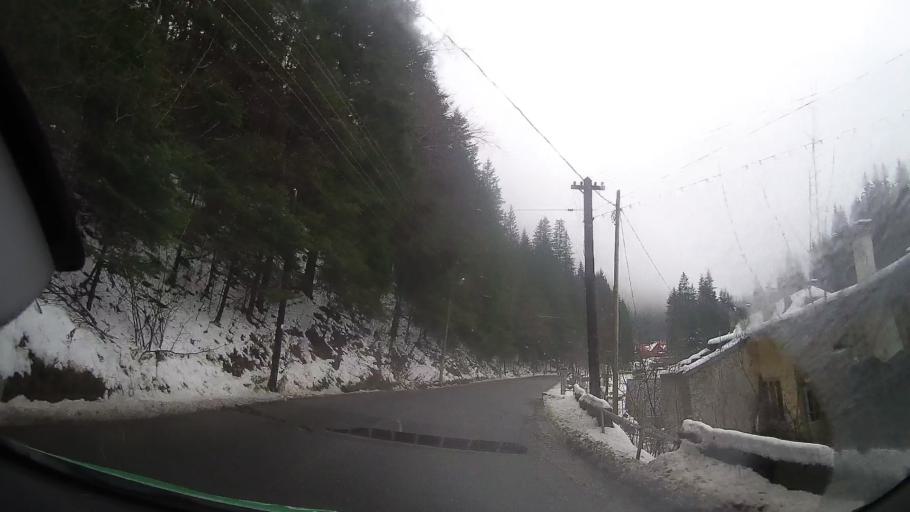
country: RO
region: Neamt
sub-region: Comuna Bicaz Chei
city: Bicaz Chei
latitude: 46.7947
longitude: 25.8008
